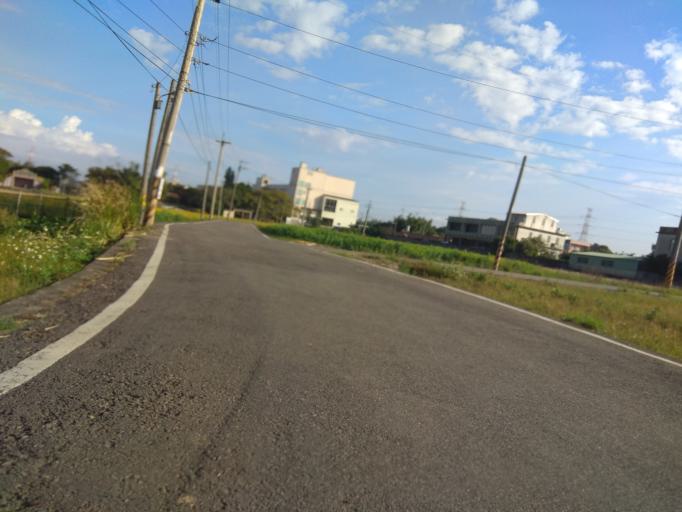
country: TW
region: Taiwan
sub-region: Hsinchu
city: Zhubei
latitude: 24.9788
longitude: 121.0636
